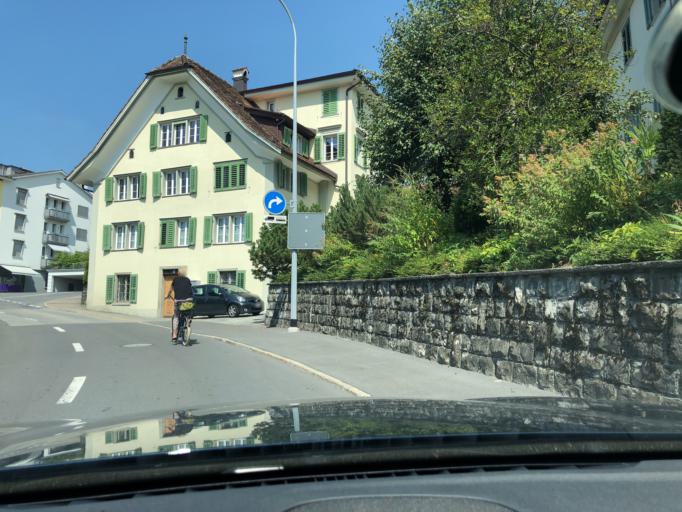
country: CH
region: Schwyz
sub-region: Bezirk Schwyz
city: Schwyz
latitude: 47.0202
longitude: 8.6578
